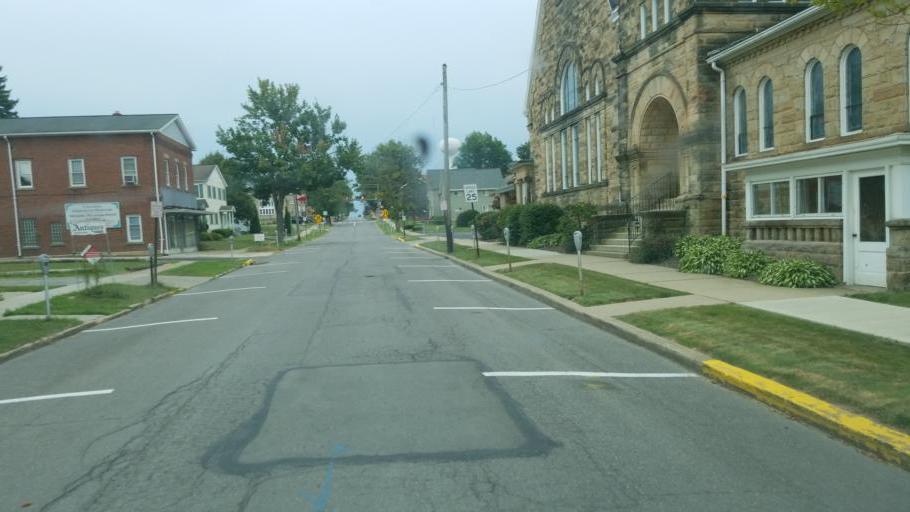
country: US
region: Pennsylvania
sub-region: Clarion County
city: Clarion
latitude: 41.2122
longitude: -79.3828
